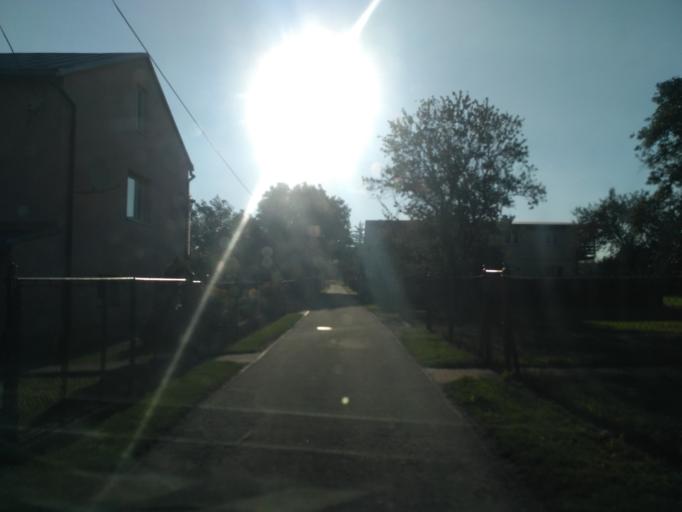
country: PL
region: Subcarpathian Voivodeship
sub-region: Powiat krosnienski
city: Dukla
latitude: 49.5554
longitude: 21.6898
